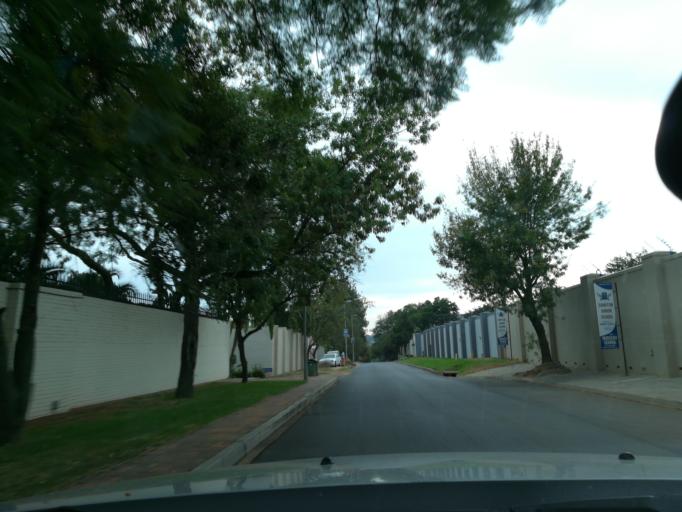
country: ZA
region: Gauteng
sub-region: City of Johannesburg Metropolitan Municipality
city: Diepsloot
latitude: -26.0672
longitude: 28.0038
